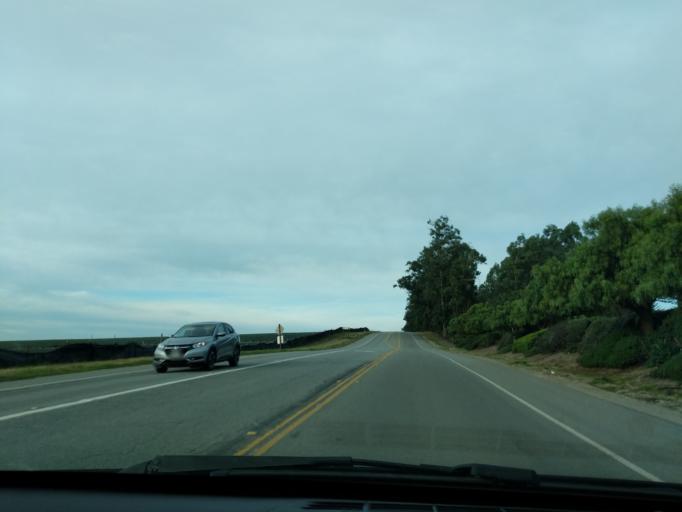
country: US
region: California
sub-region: San Luis Obispo County
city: Callender
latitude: 35.0274
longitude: -120.5611
